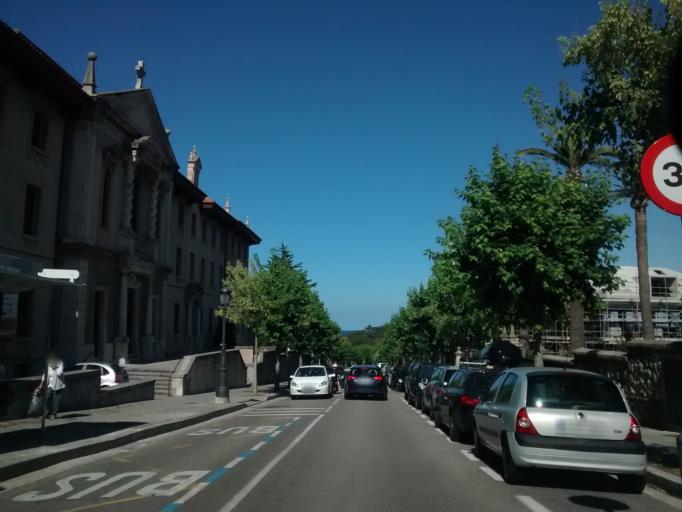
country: ES
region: Cantabria
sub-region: Provincia de Cantabria
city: Santander
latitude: 43.4675
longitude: -3.7795
